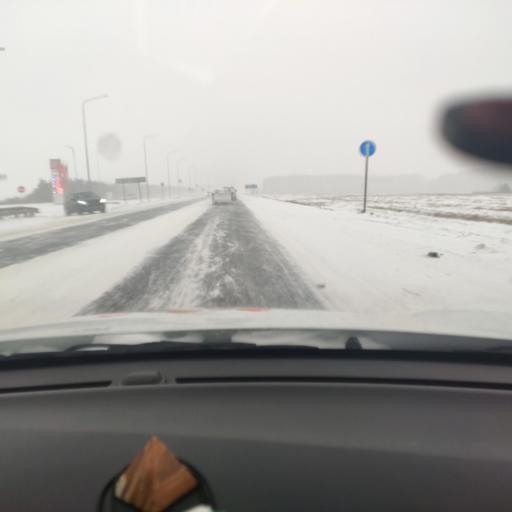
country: RU
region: Tatarstan
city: Verkhniy Uslon
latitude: 55.6597
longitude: 48.8573
